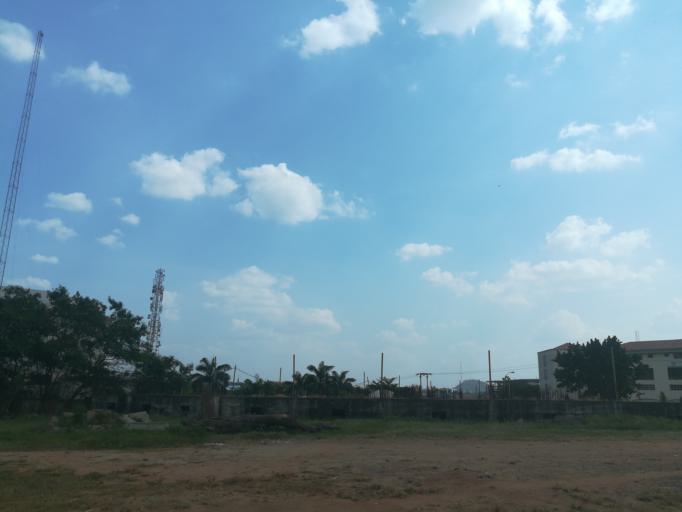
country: NG
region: Abuja Federal Capital Territory
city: Abuja
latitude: 9.0760
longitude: 7.4347
